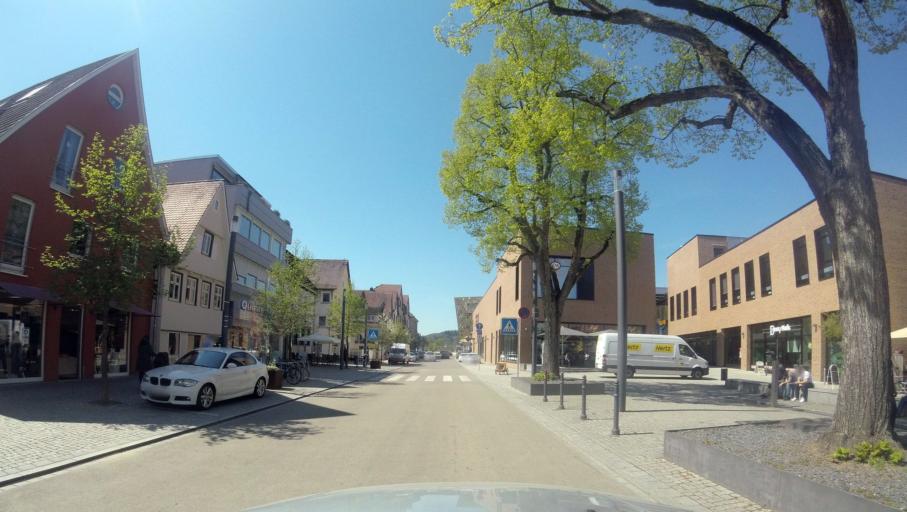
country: DE
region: Baden-Wuerttemberg
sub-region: Regierungsbezirk Stuttgart
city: Schwabisch Gmund
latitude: 48.8010
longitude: 9.7938
